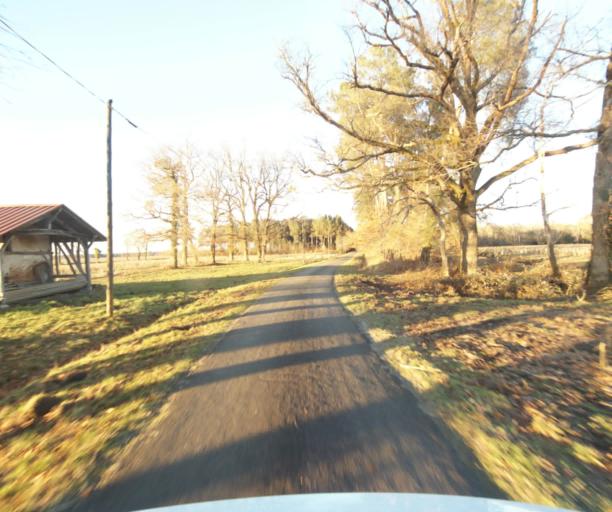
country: FR
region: Aquitaine
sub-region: Departement des Landes
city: Gabarret
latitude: 44.0921
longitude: -0.0290
